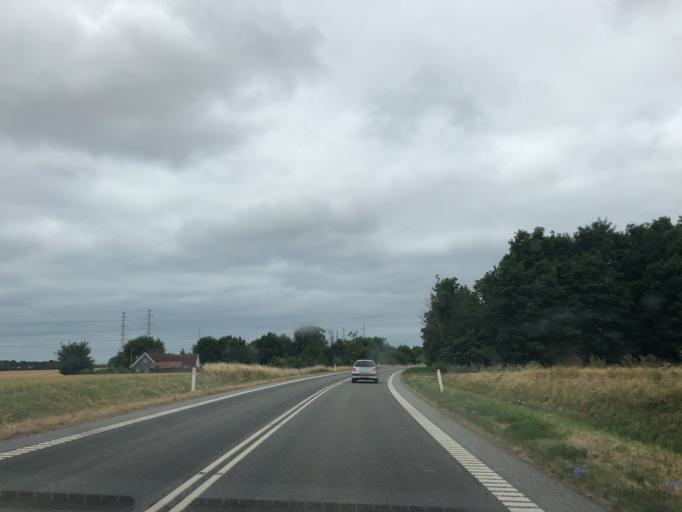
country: DK
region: Zealand
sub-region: Slagelse Kommune
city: Skaelskor
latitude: 55.2189
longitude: 11.3017
